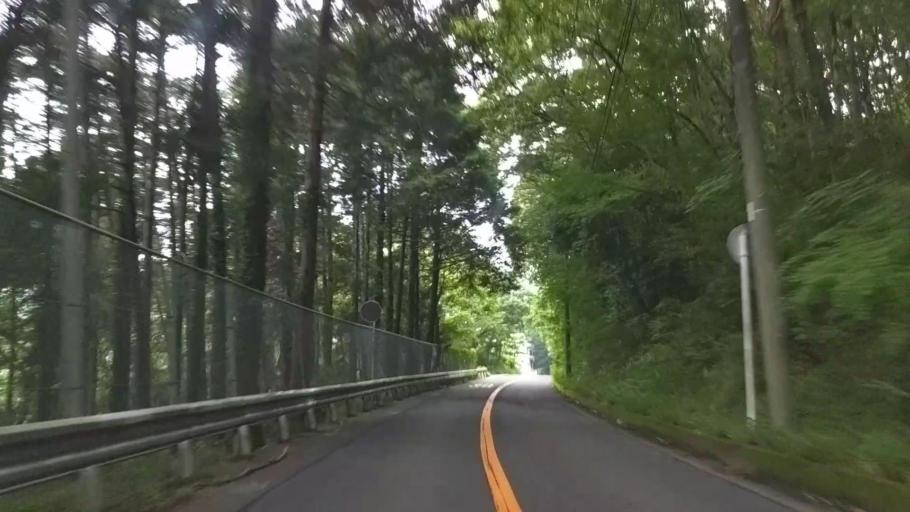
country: JP
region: Kanagawa
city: Hadano
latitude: 35.3368
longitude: 139.2367
